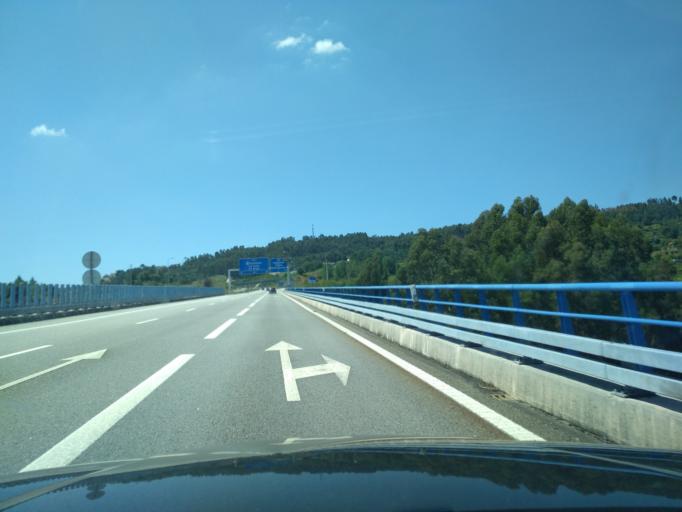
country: PT
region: Braga
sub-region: Vizela
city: Vizela
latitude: 41.4008
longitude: -8.2495
